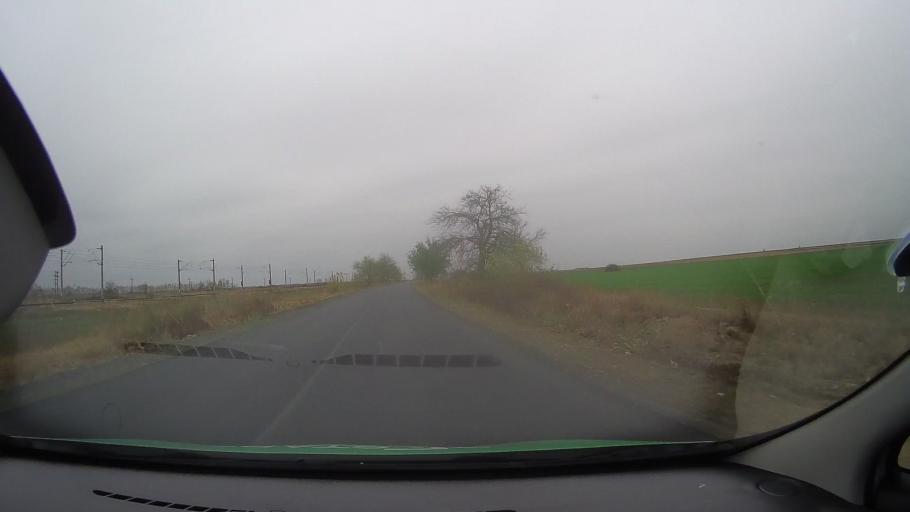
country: RO
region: Ialomita
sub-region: Comuna Valea Ciorii
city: Valea Ciorii
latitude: 44.6975
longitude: 27.6001
